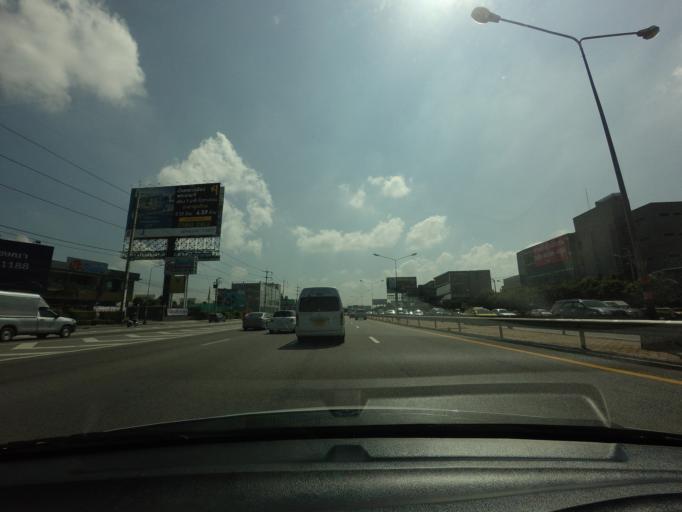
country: TH
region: Bangkok
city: Suan Luang
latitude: 13.7402
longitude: 100.6483
